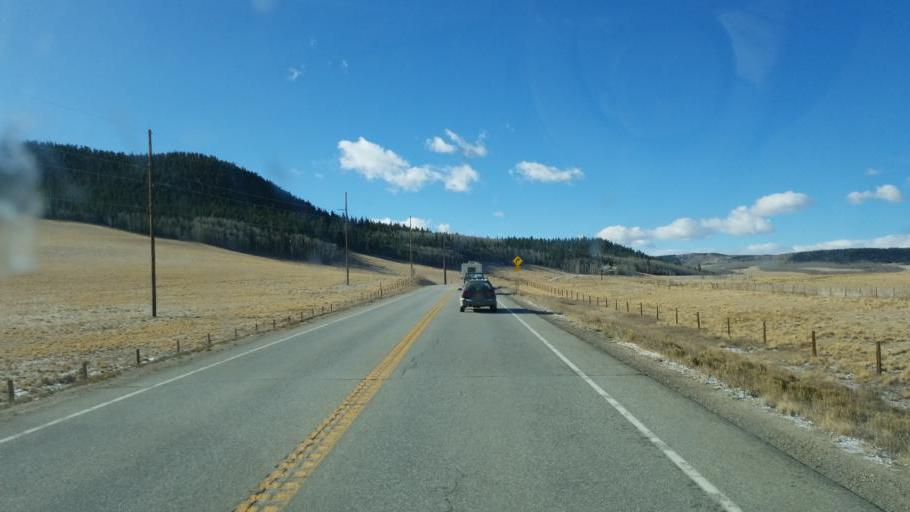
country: US
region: Colorado
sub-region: Park County
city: Fairplay
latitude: 39.2826
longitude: -105.9145
